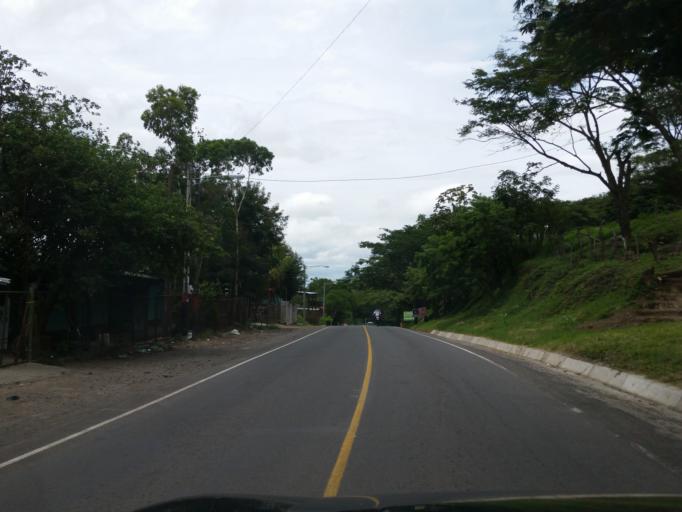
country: NI
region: Matagalpa
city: Matagalpa
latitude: 12.9412
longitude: -85.8975
